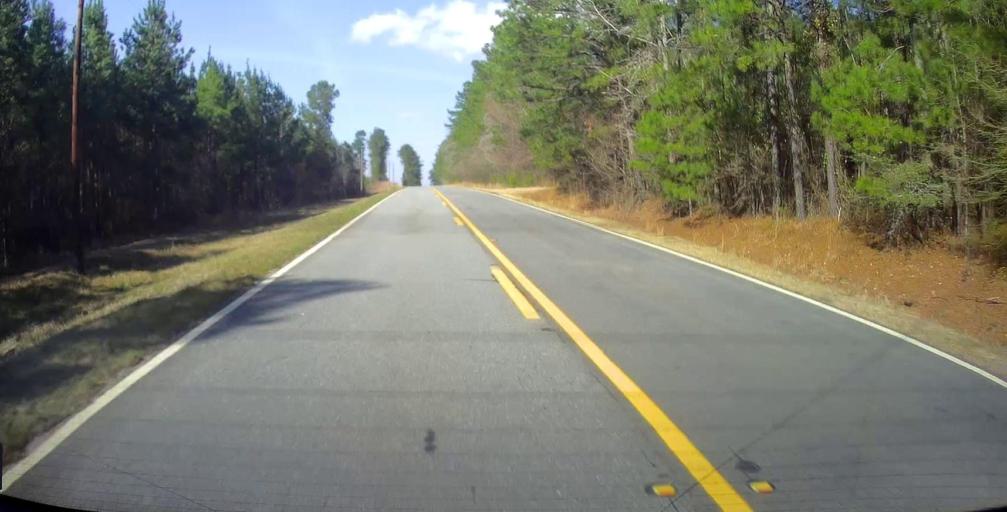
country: US
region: Georgia
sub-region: Twiggs County
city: Jeffersonville
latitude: 32.7502
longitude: -83.3435
